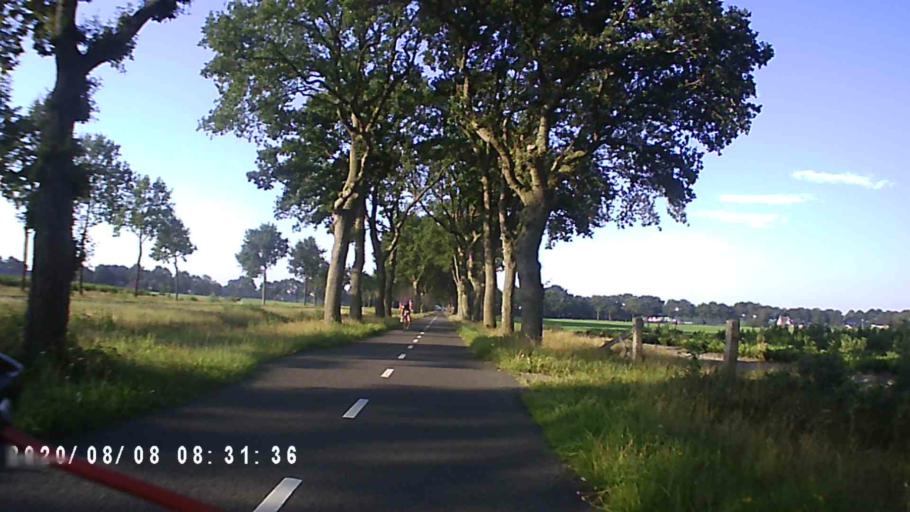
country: NL
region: Groningen
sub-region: Gemeente Leek
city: Leek
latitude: 53.0785
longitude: 6.3347
